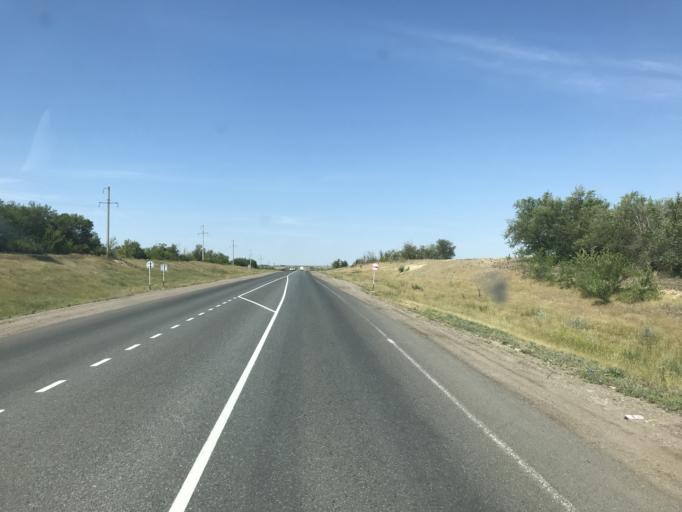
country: KZ
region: Aqtoebe
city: Aqtobe
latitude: 50.2372
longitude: 56.6767
